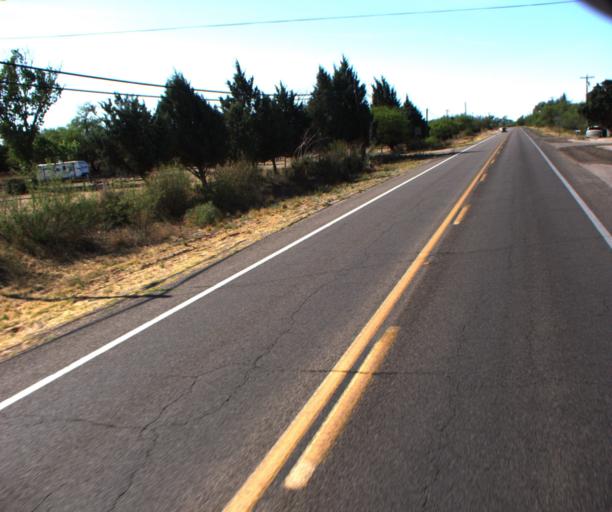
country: US
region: Arizona
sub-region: Cochise County
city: Saint David
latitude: 31.8886
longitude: -110.2135
